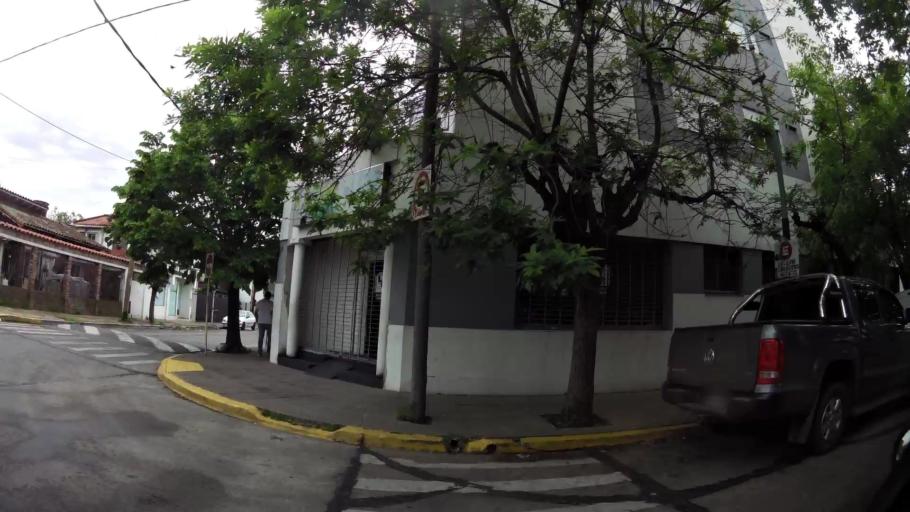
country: AR
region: Buenos Aires
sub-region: Partido de Quilmes
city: Quilmes
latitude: -34.7643
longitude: -58.2055
